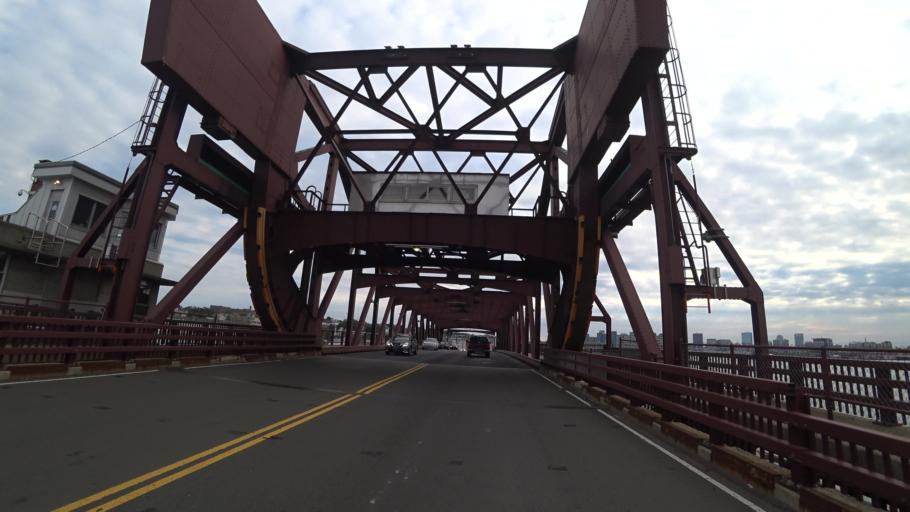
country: US
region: Massachusetts
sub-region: Suffolk County
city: Chelsea
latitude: 42.3862
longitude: -71.0394
